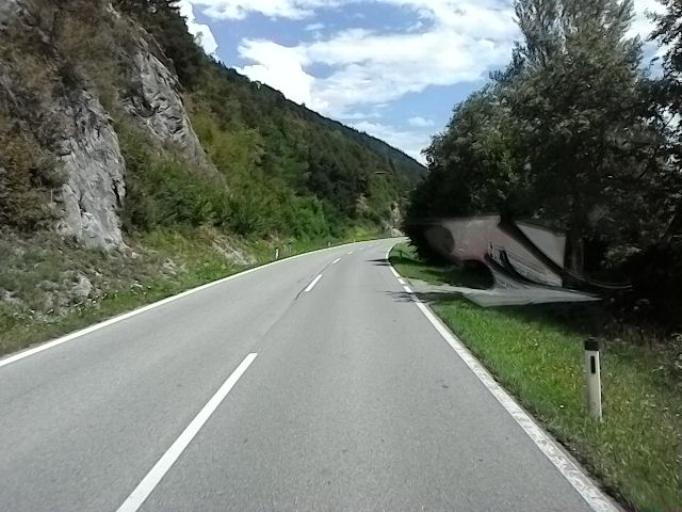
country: AT
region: Tyrol
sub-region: Politischer Bezirk Innsbruck Land
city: Inzing
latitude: 47.2874
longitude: 11.1813
